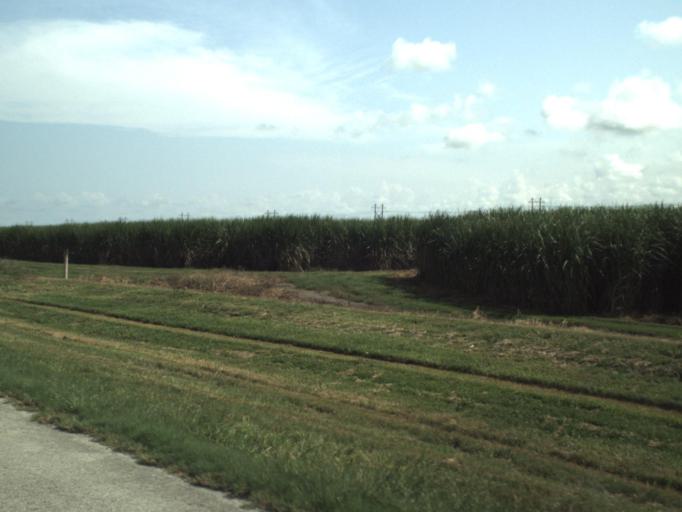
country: US
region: Florida
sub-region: Palm Beach County
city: Belle Glade
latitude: 26.7525
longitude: -80.6829
